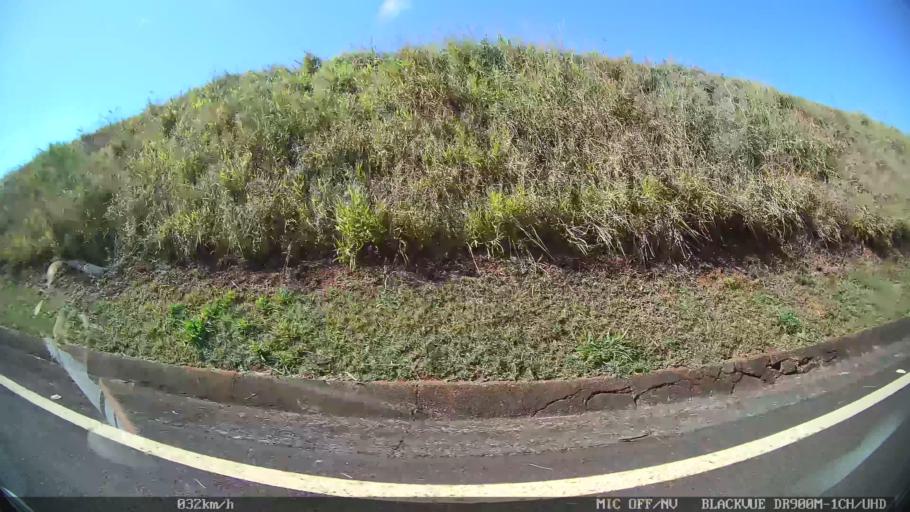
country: BR
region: Sao Paulo
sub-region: Franca
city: Franca
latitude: -20.6799
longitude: -47.4958
